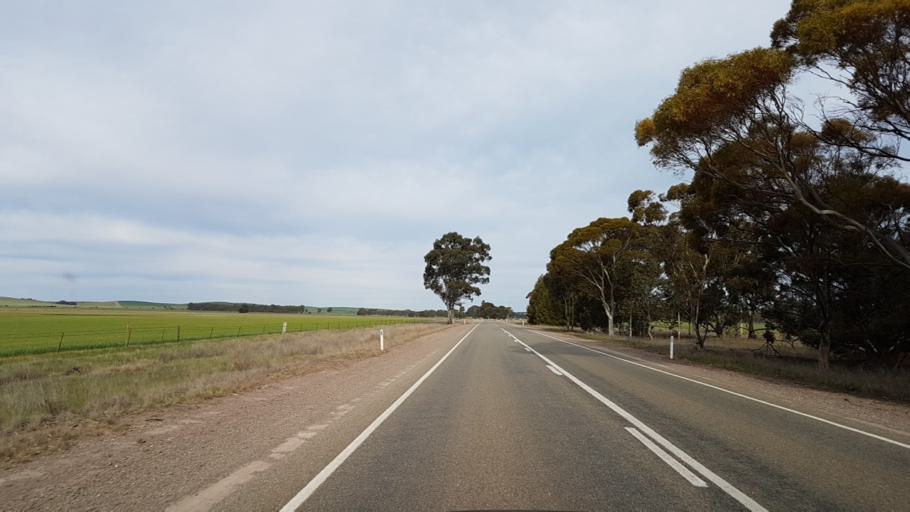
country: AU
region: South Australia
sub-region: Northern Areas
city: Jamestown
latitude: -33.1876
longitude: 138.5049
